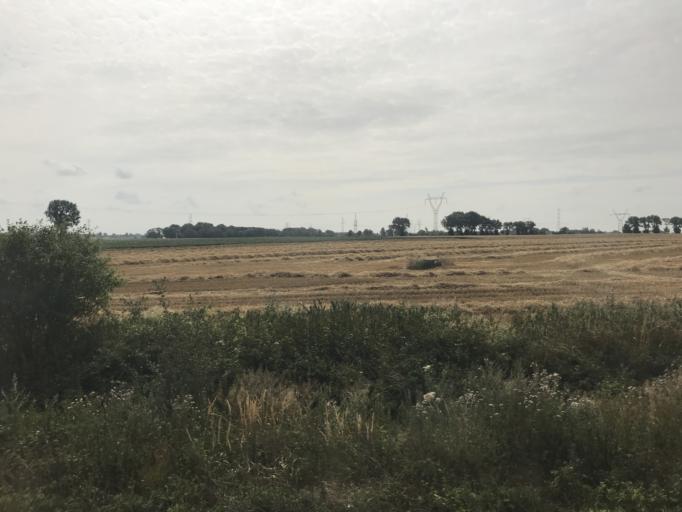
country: PL
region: Kujawsko-Pomorskie
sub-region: Powiat inowroclawski
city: Janikowo
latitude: 52.7701
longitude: 18.1410
